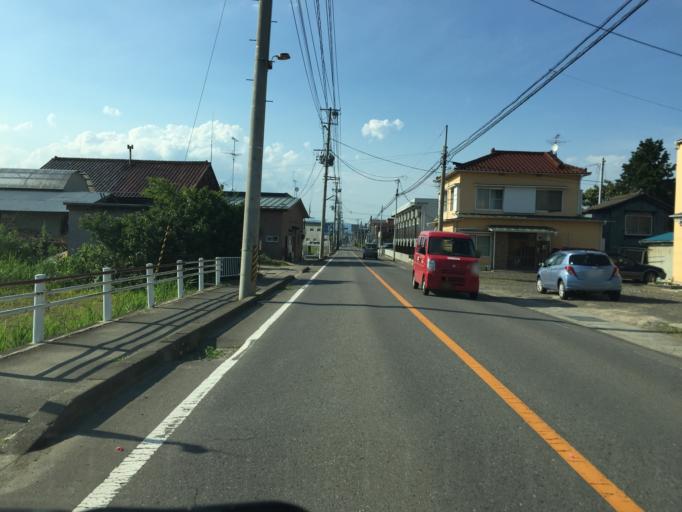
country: JP
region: Fukushima
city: Motomiya
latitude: 37.5047
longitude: 140.4017
